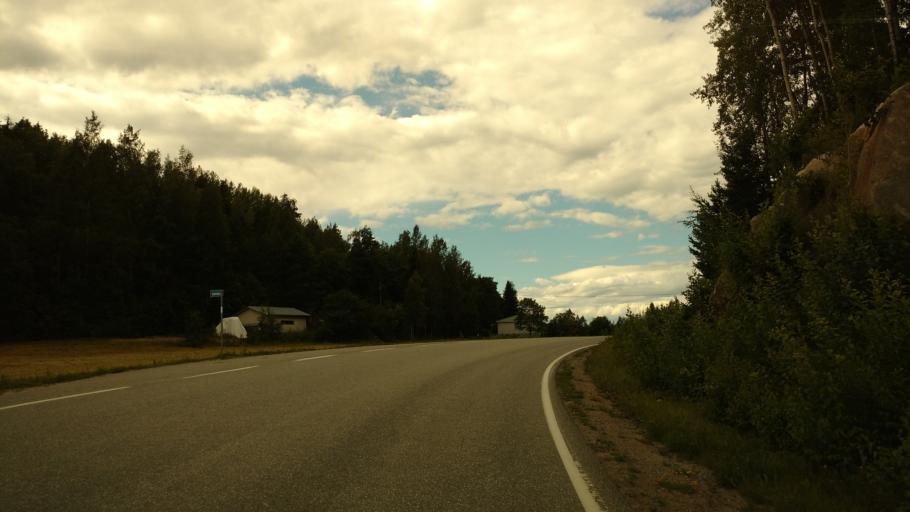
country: FI
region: Varsinais-Suomi
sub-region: Salo
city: Halikko
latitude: 60.4002
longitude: 23.0180
